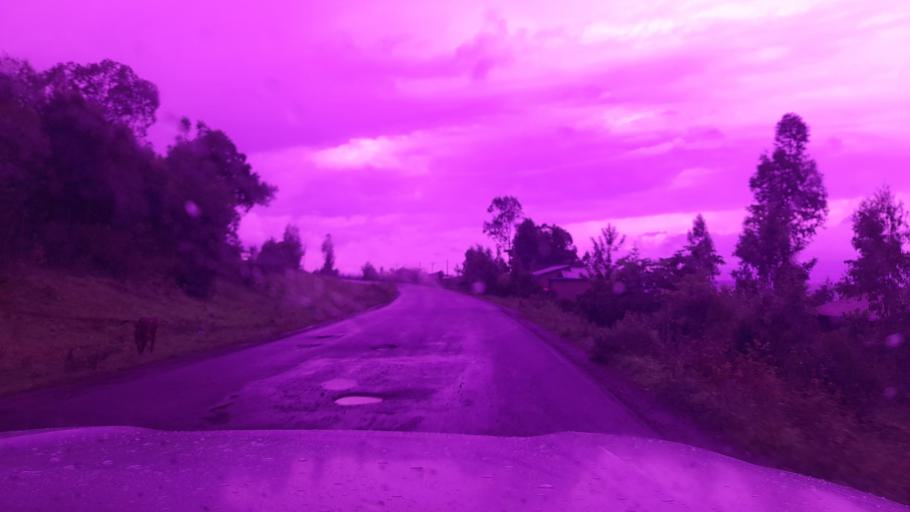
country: ET
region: Oromiya
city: Jima
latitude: 7.7064
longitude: 37.0684
